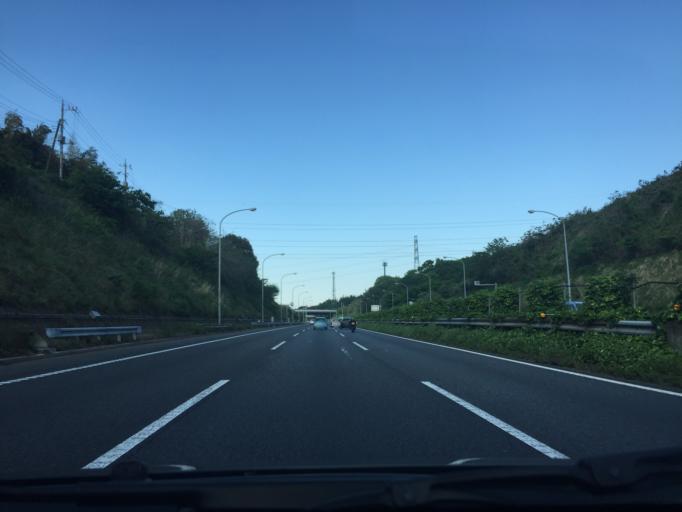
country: JP
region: Tokyo
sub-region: Machida-shi
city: Machida
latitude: 35.5147
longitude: 139.4921
